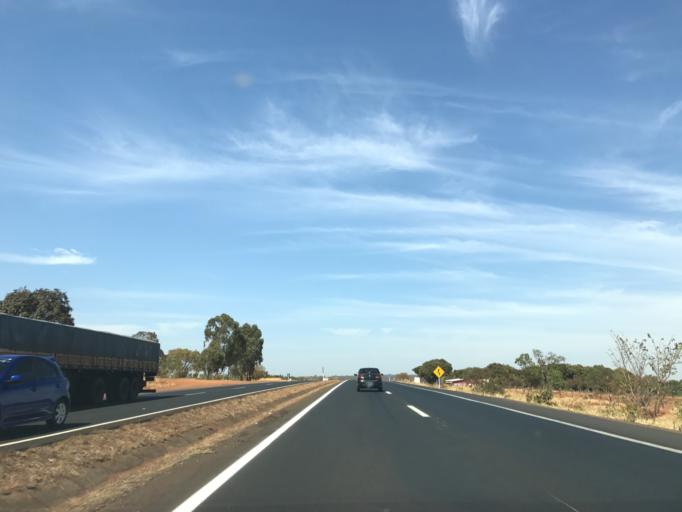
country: BR
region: Minas Gerais
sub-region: Monte Alegre De Minas
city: Monte Alegre de Minas
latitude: -18.8087
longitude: -49.0847
